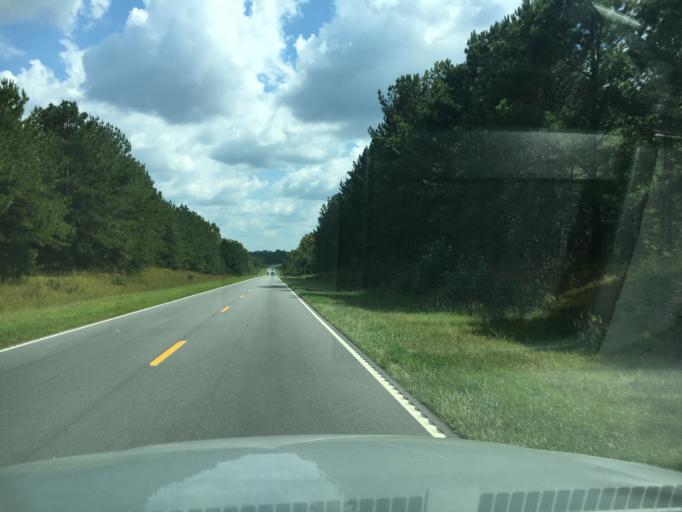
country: US
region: South Carolina
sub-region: Greenwood County
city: Greenwood
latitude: 34.1545
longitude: -82.1675
